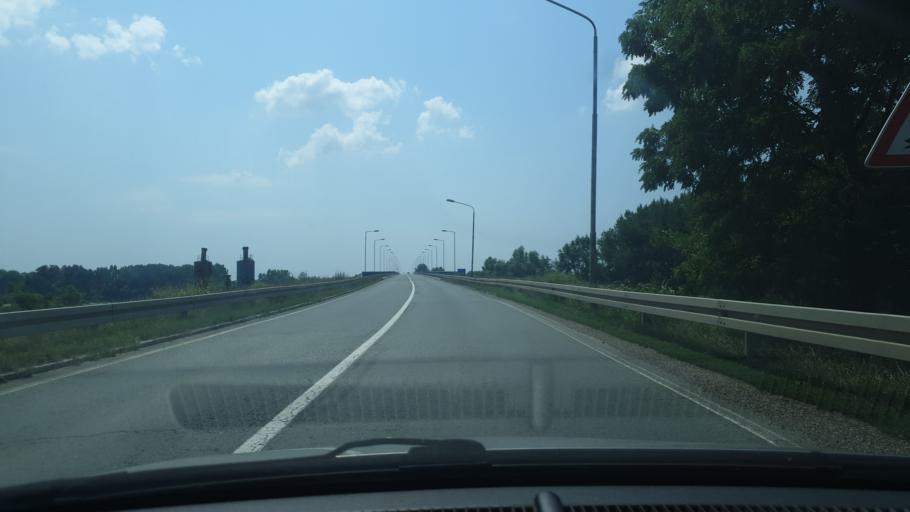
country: RS
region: Autonomna Pokrajina Vojvodina
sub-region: Sremski Okrug
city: Sremska Mitrovica
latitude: 44.9638
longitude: 19.6310
